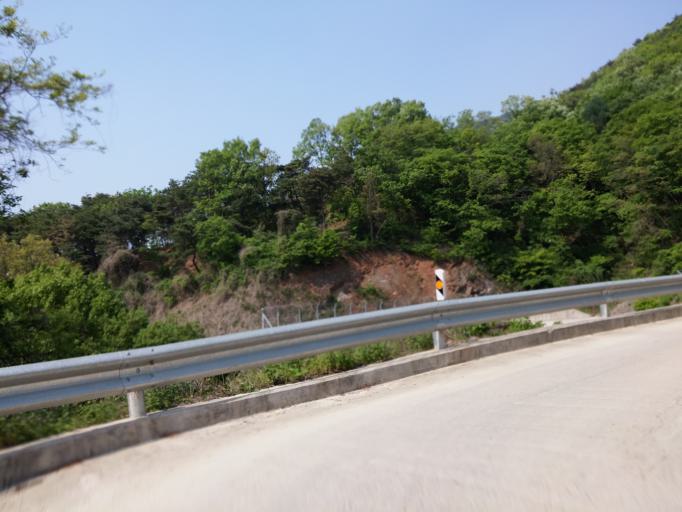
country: KR
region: Chungcheongbuk-do
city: Okcheon
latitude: 36.3781
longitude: 127.6046
